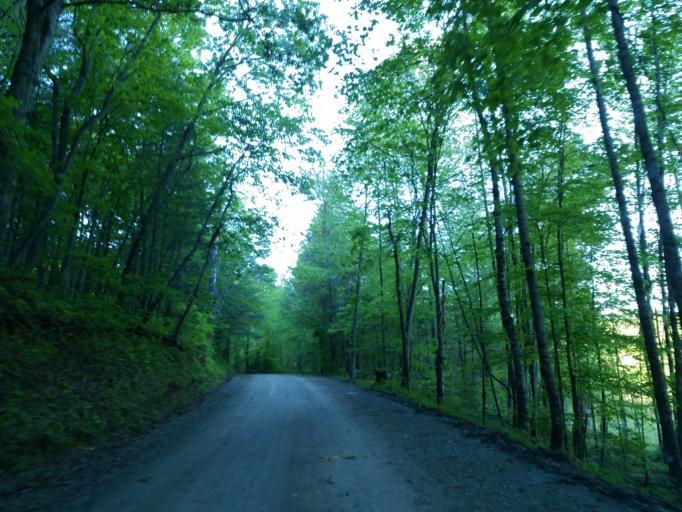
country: US
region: Georgia
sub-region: Fannin County
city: Blue Ridge
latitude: 34.7501
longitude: -84.2766
